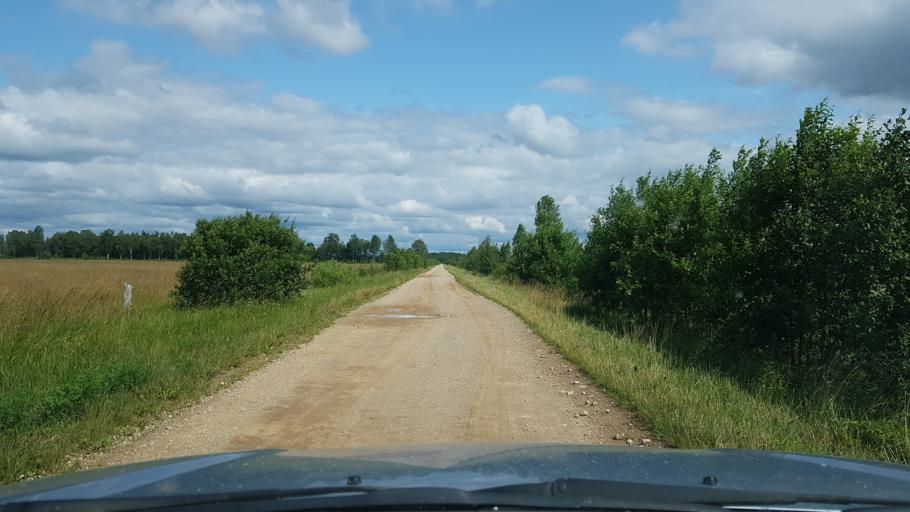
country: EE
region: Ida-Virumaa
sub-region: Sillamaee linn
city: Sillamae
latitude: 59.3703
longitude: 27.9043
